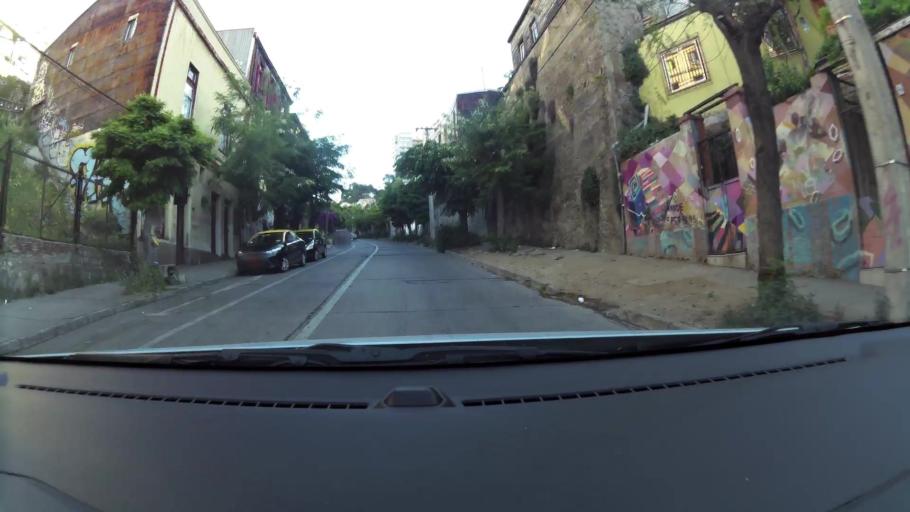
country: CL
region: Valparaiso
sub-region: Provincia de Valparaiso
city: Valparaiso
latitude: -33.0464
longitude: -71.6237
